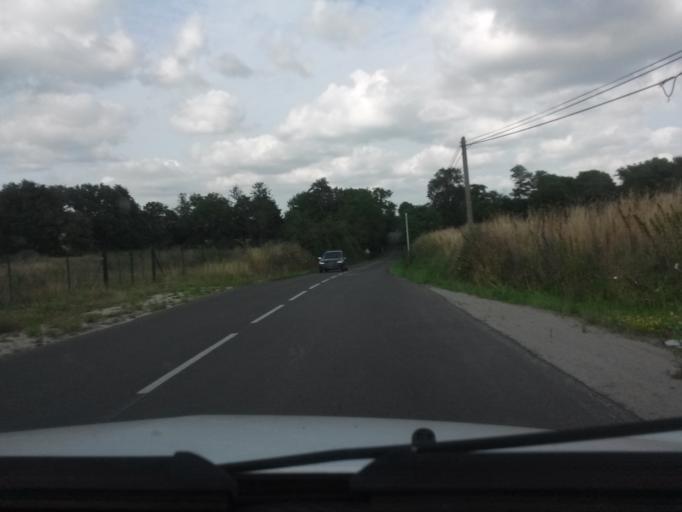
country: FR
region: Pays de la Loire
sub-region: Departement de la Vendee
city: La Bruffiere
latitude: 47.0131
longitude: -1.1813
